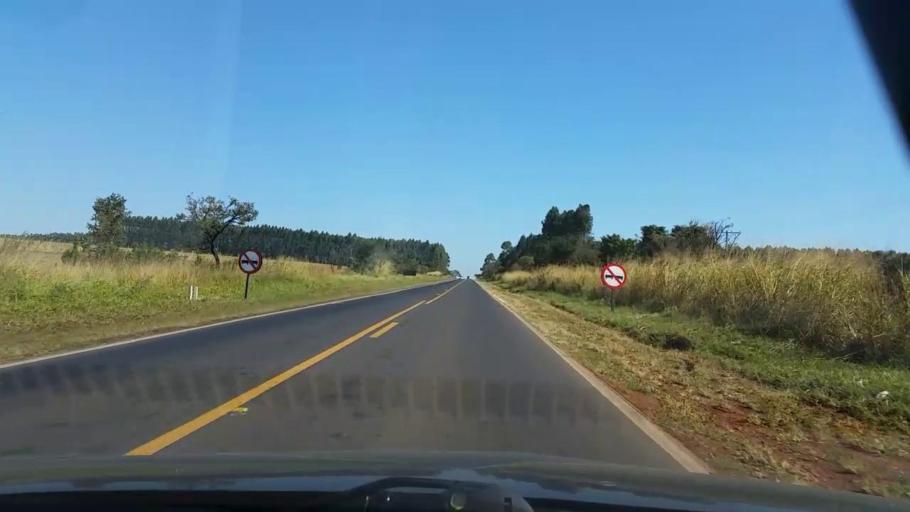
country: BR
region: Sao Paulo
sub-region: Avare
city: Avare
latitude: -22.9180
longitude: -48.7810
